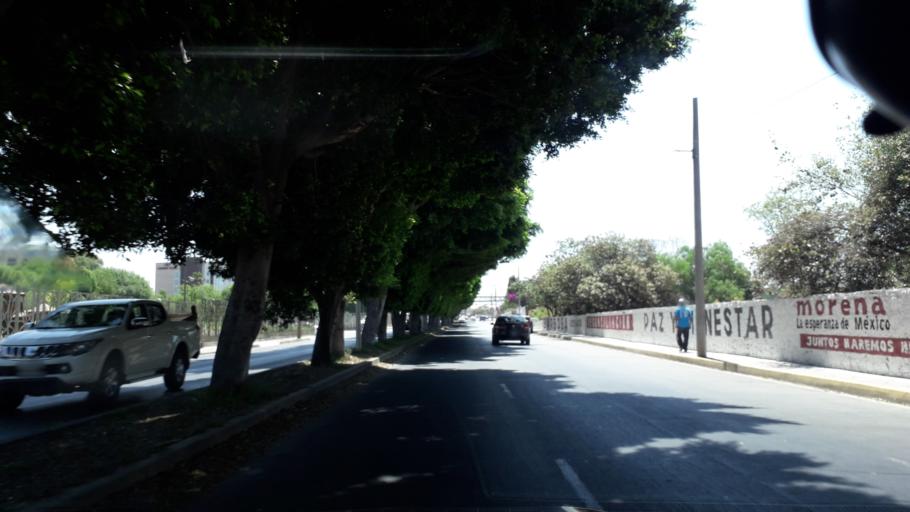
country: MX
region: Puebla
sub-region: Cuautlancingo
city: Sanctorum
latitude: 19.0916
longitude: -98.2322
